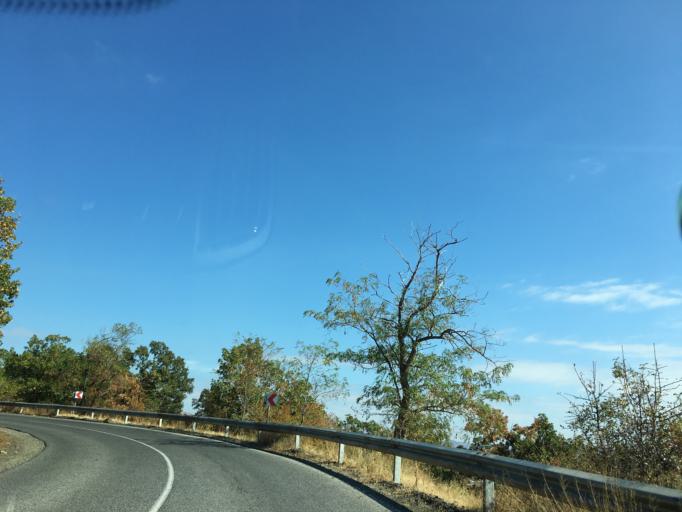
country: BG
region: Kurdzhali
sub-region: Obshtina Krumovgrad
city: Krumovgrad
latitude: 41.4784
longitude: 25.5534
